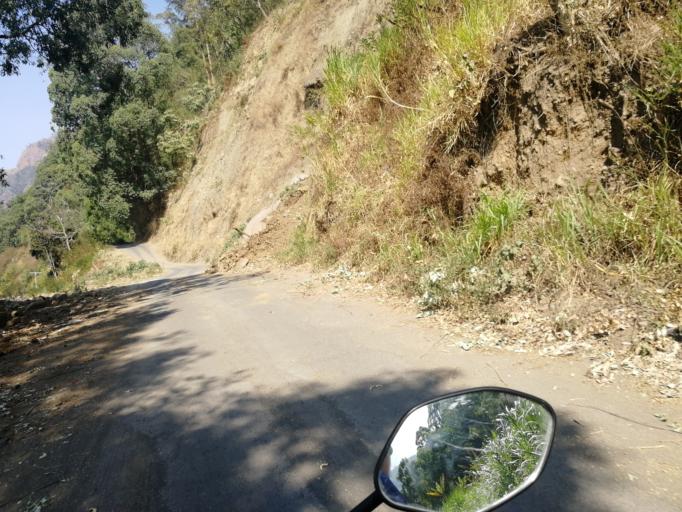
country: ID
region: Bali
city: Banjar Buahan
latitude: -8.2868
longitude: 115.3983
